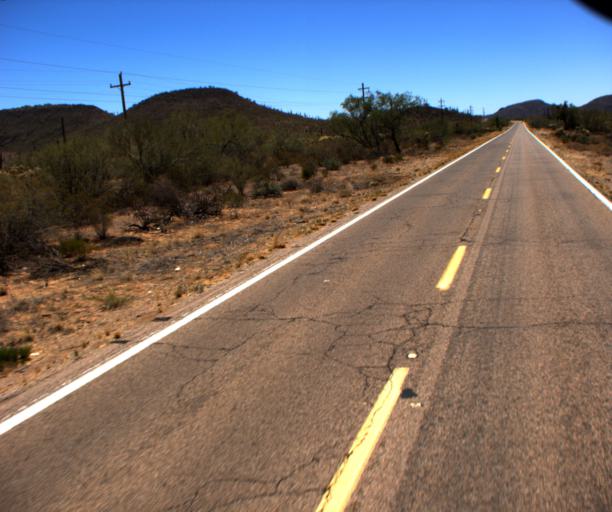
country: US
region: Arizona
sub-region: Pima County
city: Sells
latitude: 31.9903
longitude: -111.9775
